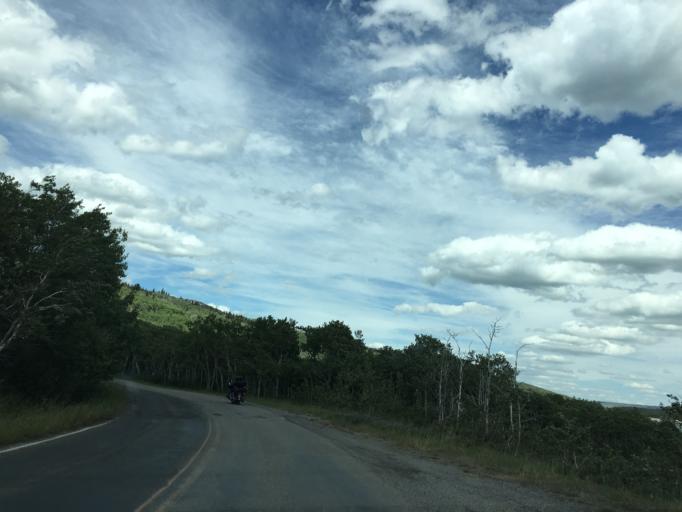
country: CA
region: Alberta
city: Cardston
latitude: 48.8272
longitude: -113.5513
